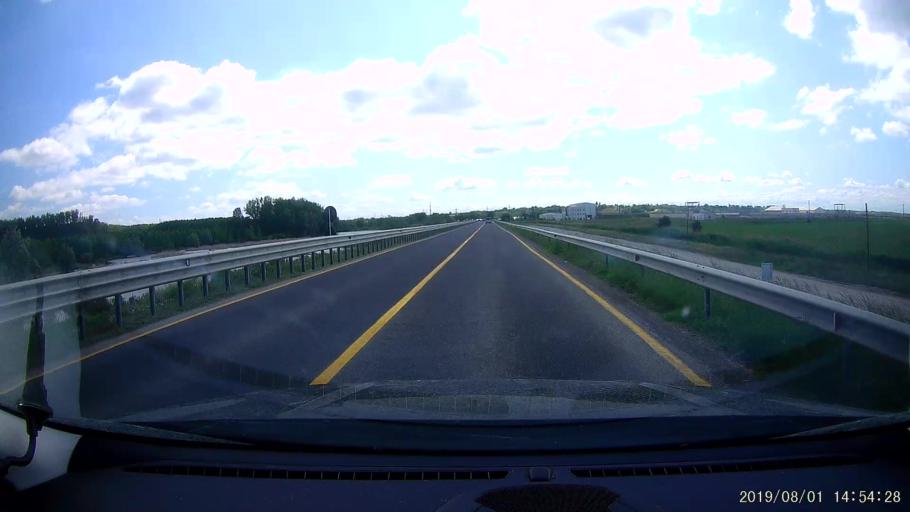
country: RO
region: Braila
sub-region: Municipiul Braila
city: Braila
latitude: 45.3178
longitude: 27.9883
